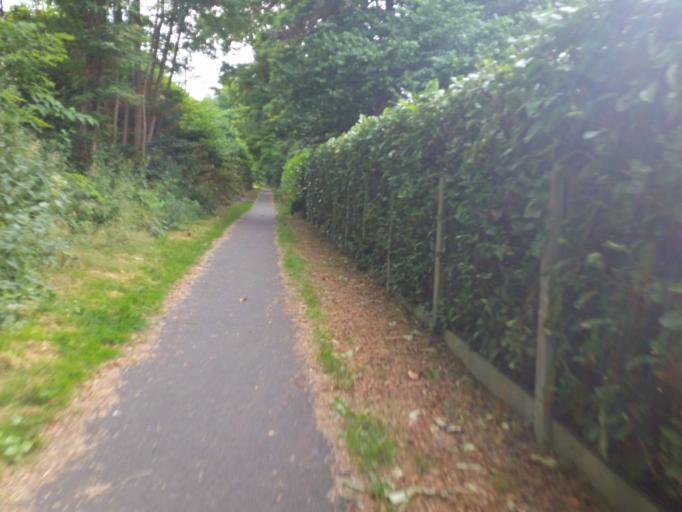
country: BE
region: Flanders
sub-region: Provincie Antwerpen
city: Bonheiden
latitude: 50.9936
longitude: 4.5119
